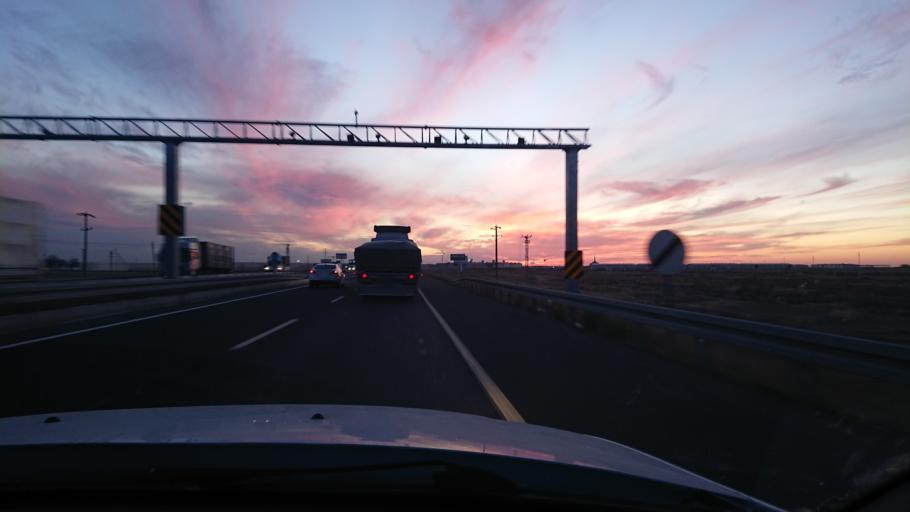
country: TR
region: Aksaray
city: Aksaray
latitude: 38.3411
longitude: 33.9463
